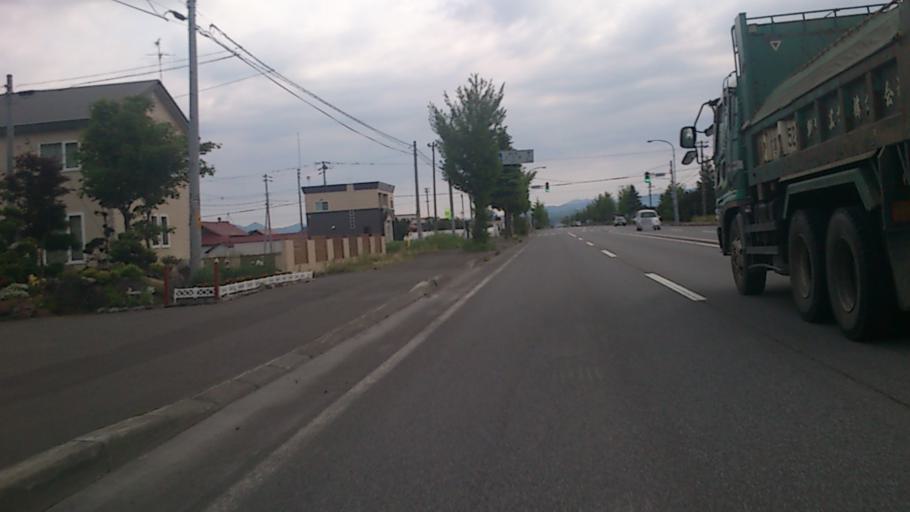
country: JP
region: Hokkaido
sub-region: Asahikawa-shi
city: Asahikawa
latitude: 43.8375
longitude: 142.4770
